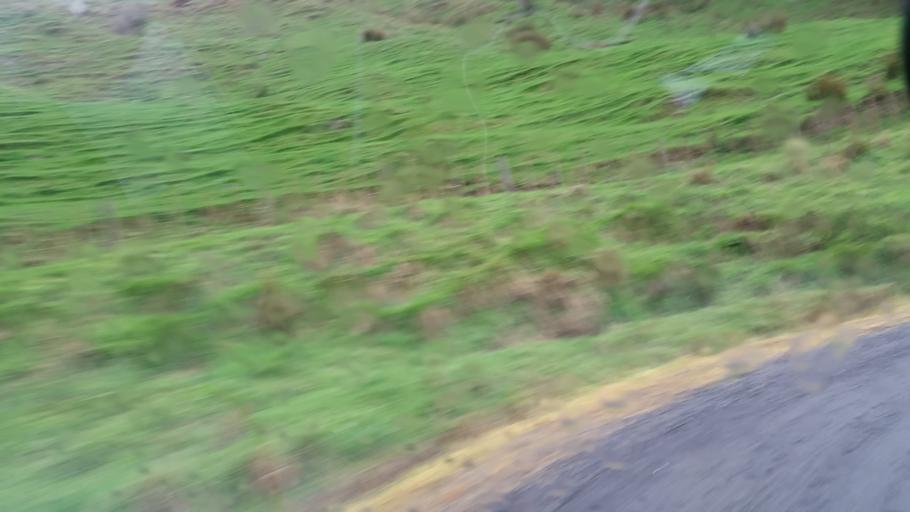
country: NZ
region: Taranaki
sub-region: South Taranaki District
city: Eltham
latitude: -39.4707
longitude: 174.4196
